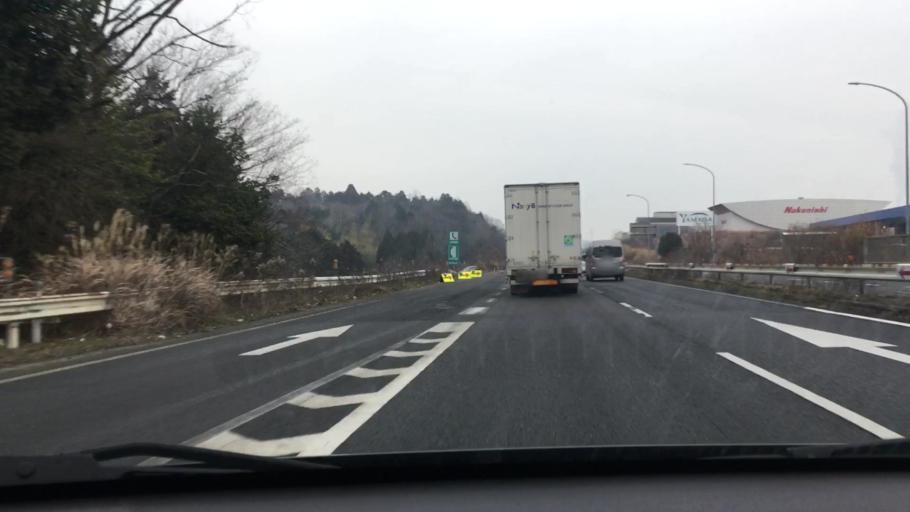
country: JP
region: Mie
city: Ueno-ebisumachi
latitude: 34.7075
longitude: 136.0767
